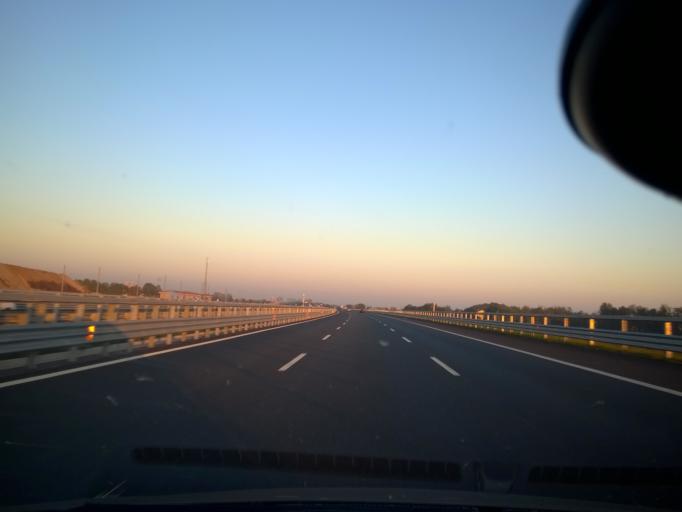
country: IT
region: Lombardy
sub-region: Provincia di Bergamo
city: Calvenzano
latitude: 45.5032
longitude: 9.5892
